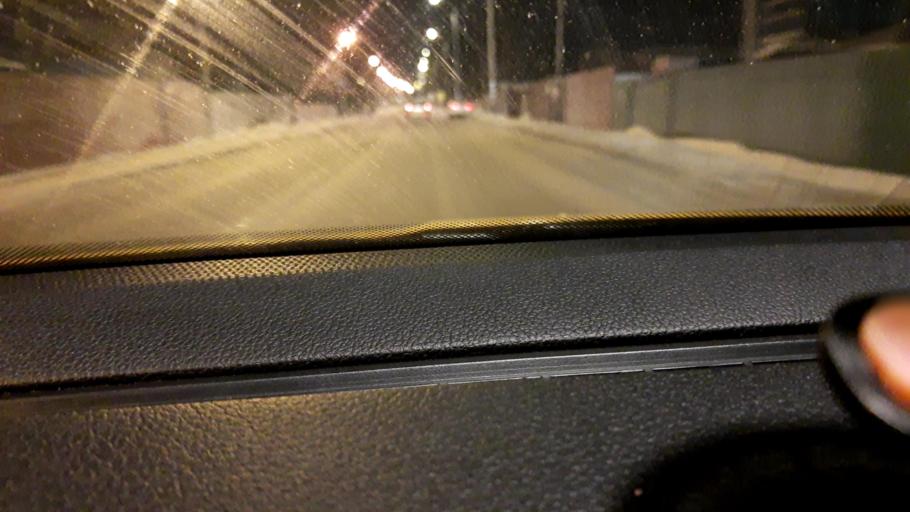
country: RU
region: Moskovskaya
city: Nakhabino
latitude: 55.8433
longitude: 37.1866
